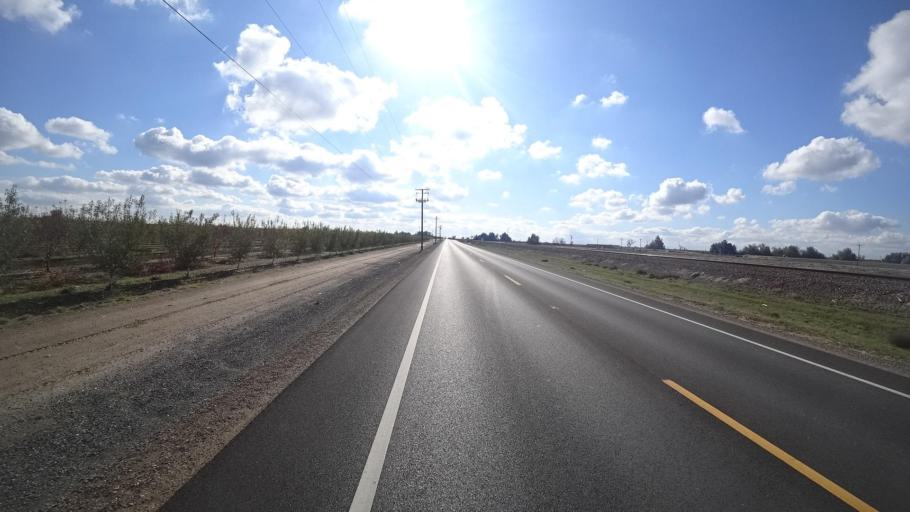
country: US
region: California
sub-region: Kern County
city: Wasco
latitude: 35.6696
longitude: -119.3308
